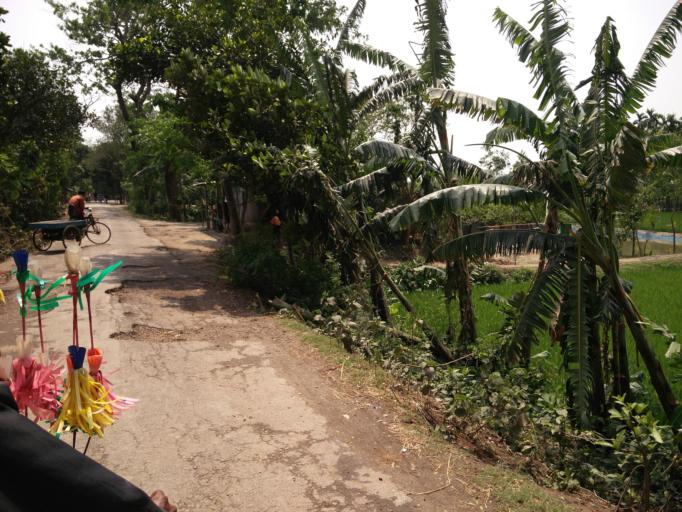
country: BD
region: Dhaka
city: Sherpur
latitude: 24.9402
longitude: 90.1599
